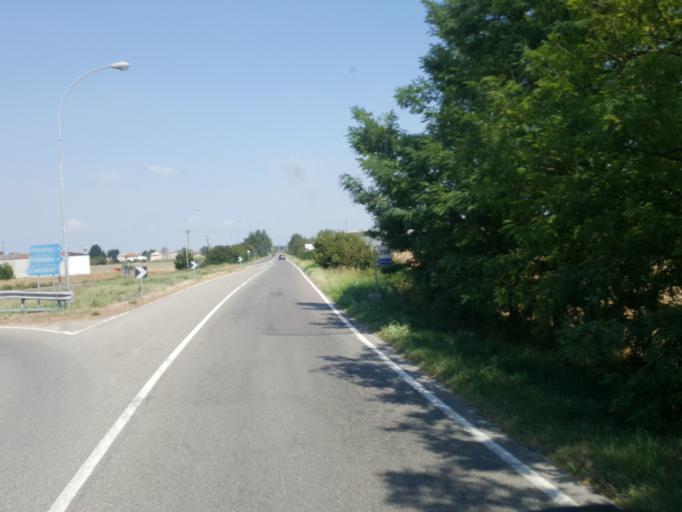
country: IT
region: Emilia-Romagna
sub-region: Provincia di Piacenza
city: Caorso
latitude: 45.0675
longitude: 9.8884
